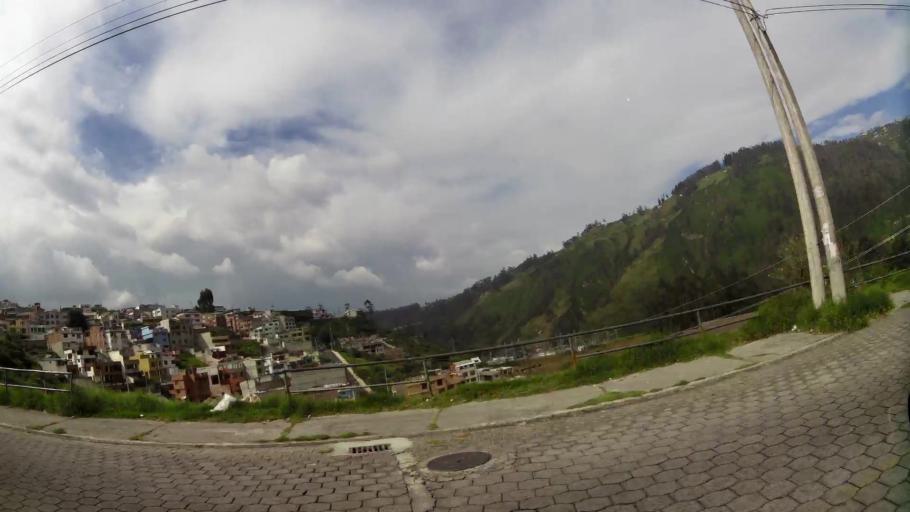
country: EC
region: Pichincha
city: Quito
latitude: -0.2164
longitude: -78.4849
